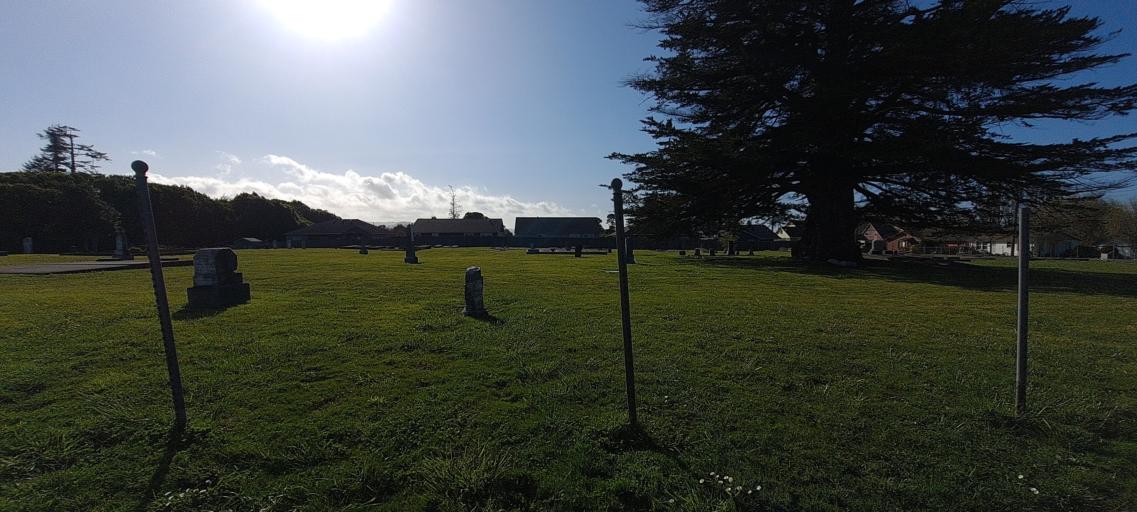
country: US
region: California
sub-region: Humboldt County
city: Fortuna
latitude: 40.5734
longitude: -124.1330
